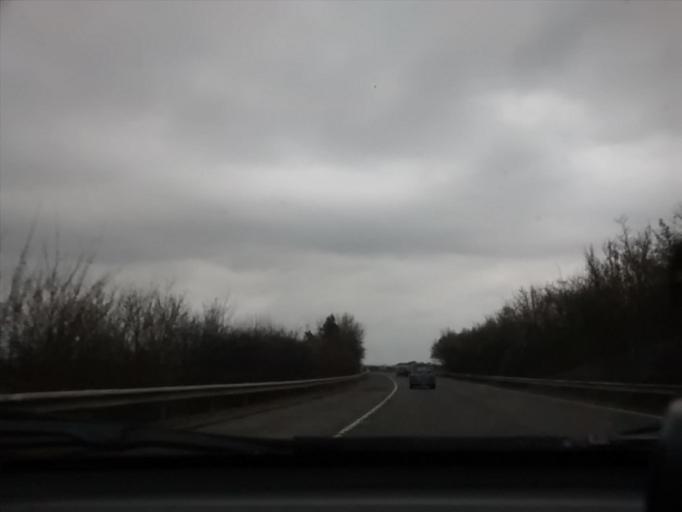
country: GB
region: England
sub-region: Cambridgeshire
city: Duxford
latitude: 52.0626
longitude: 0.1865
